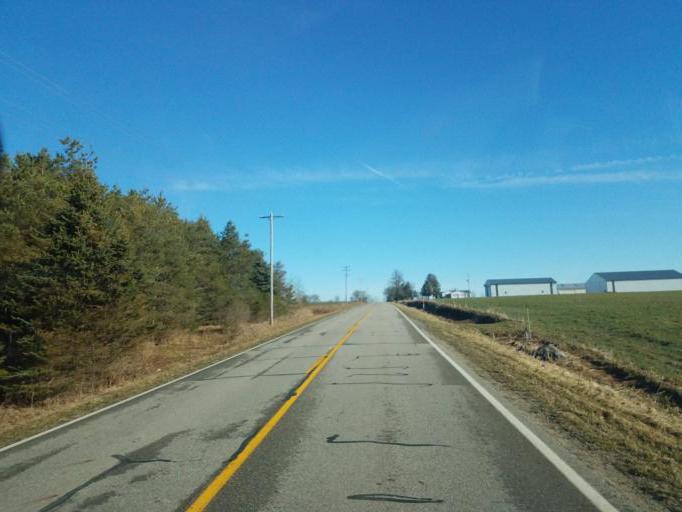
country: US
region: Michigan
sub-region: Montcalm County
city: Edmore
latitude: 43.4778
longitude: -85.0850
